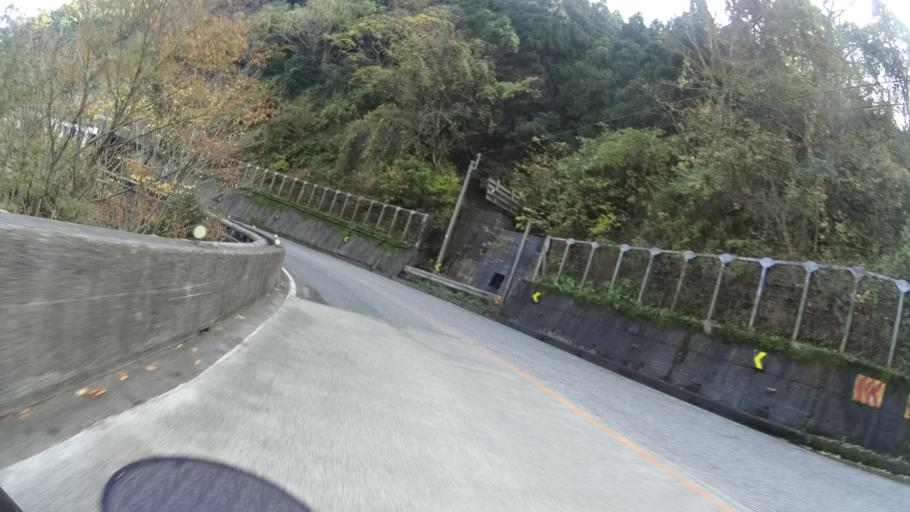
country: JP
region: Niigata
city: Itoigawa
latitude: 36.9936
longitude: 137.7034
